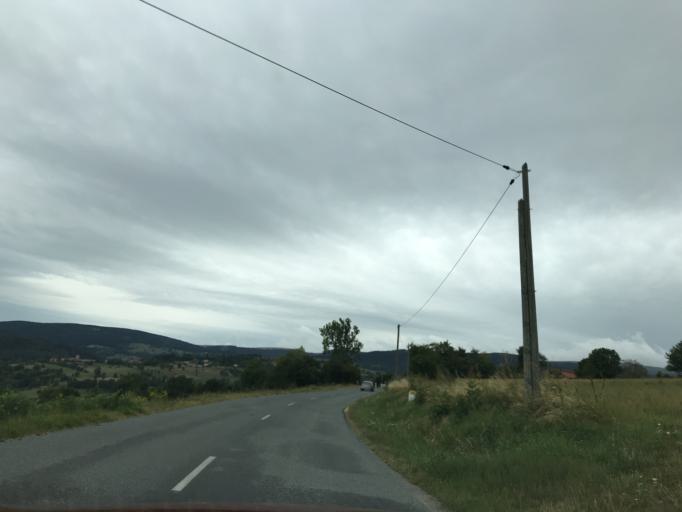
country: FR
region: Rhone-Alpes
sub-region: Departement de la Loire
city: Sail-sous-Couzan
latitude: 45.6947
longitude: 3.9116
